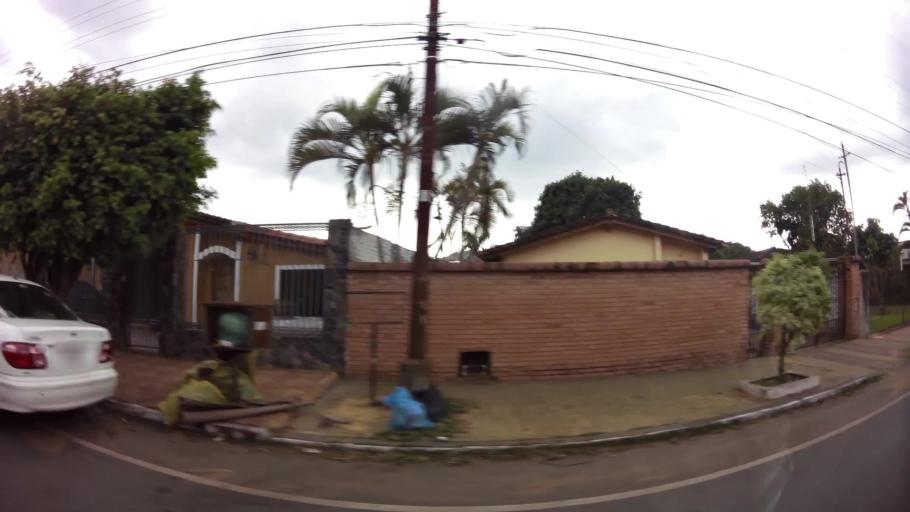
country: PY
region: Central
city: Fernando de la Mora
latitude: -25.3315
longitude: -57.5557
